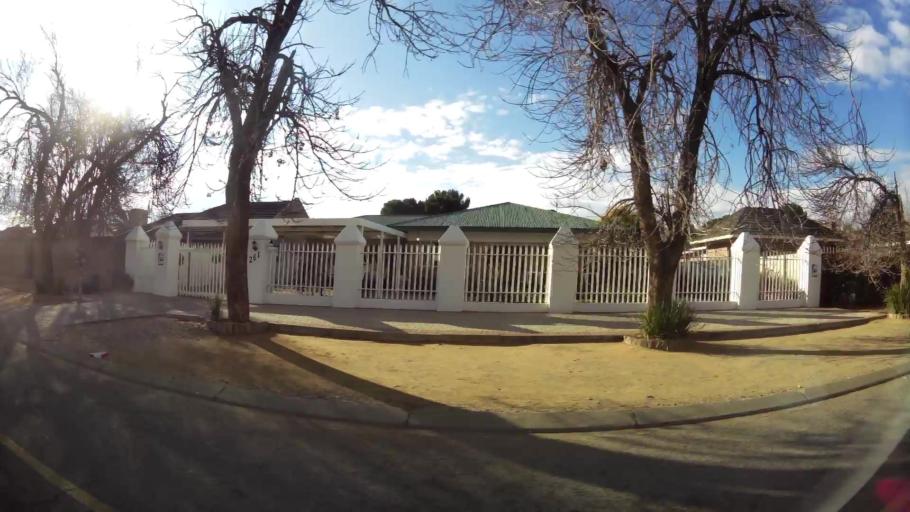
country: ZA
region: Orange Free State
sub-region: Lejweleputswa District Municipality
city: Welkom
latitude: -27.9822
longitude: 26.7196
